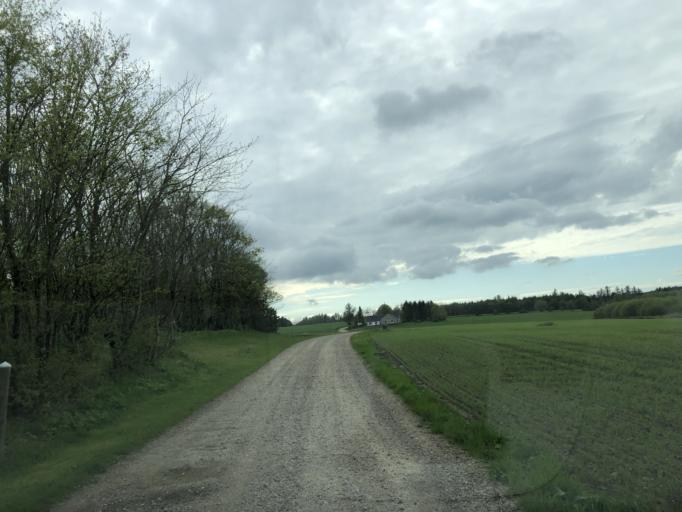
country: DK
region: Central Jutland
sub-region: Holstebro Kommune
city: Ulfborg
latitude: 56.1972
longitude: 8.4498
